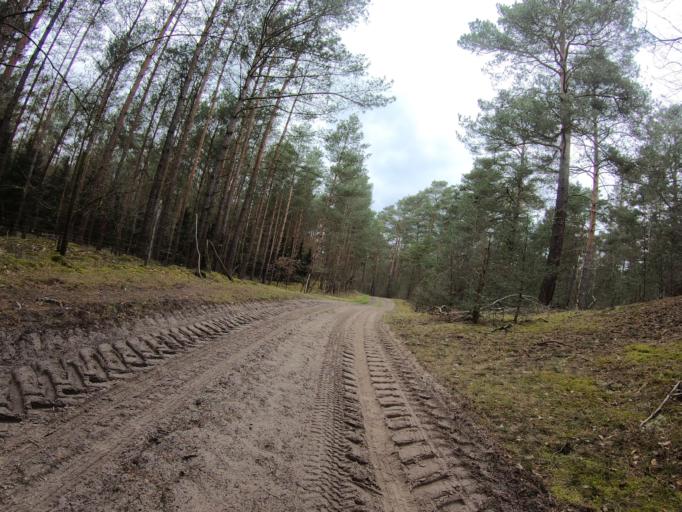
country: DE
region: Lower Saxony
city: Leiferde
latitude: 52.4860
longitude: 10.4488
